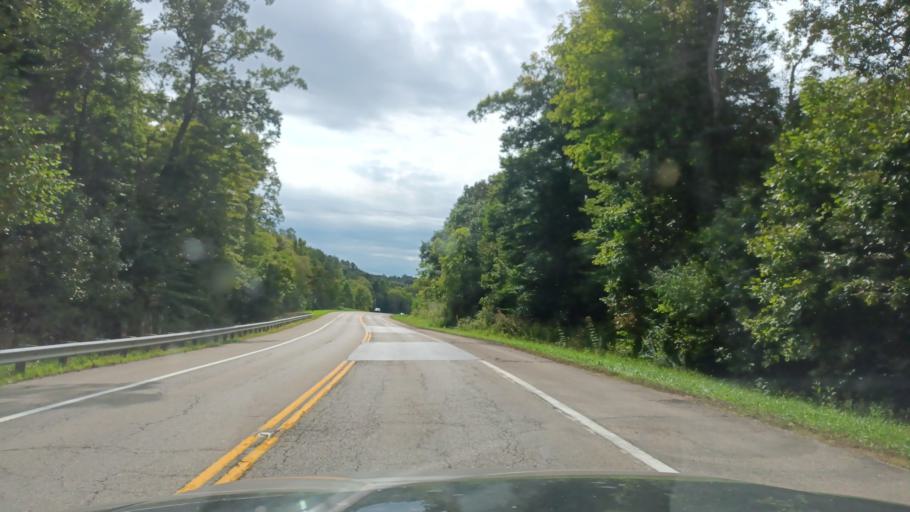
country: US
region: Ohio
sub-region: Vinton County
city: McArthur
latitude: 39.2748
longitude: -82.5548
